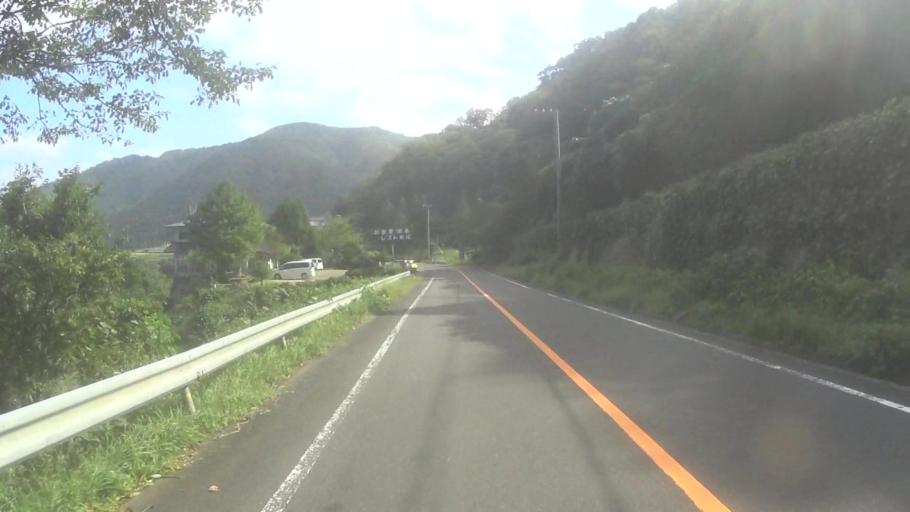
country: JP
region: Kyoto
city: Miyazu
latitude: 35.7501
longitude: 135.1401
